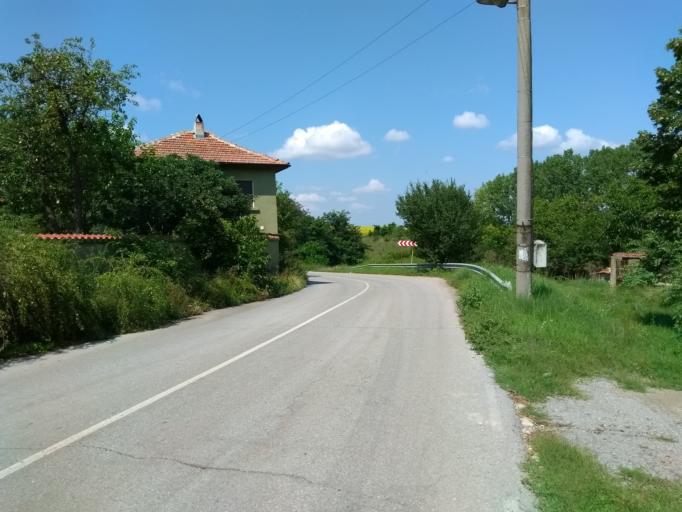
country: BG
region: Sliven
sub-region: Obshtina Sliven
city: Kermen
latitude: 42.4575
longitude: 26.1362
